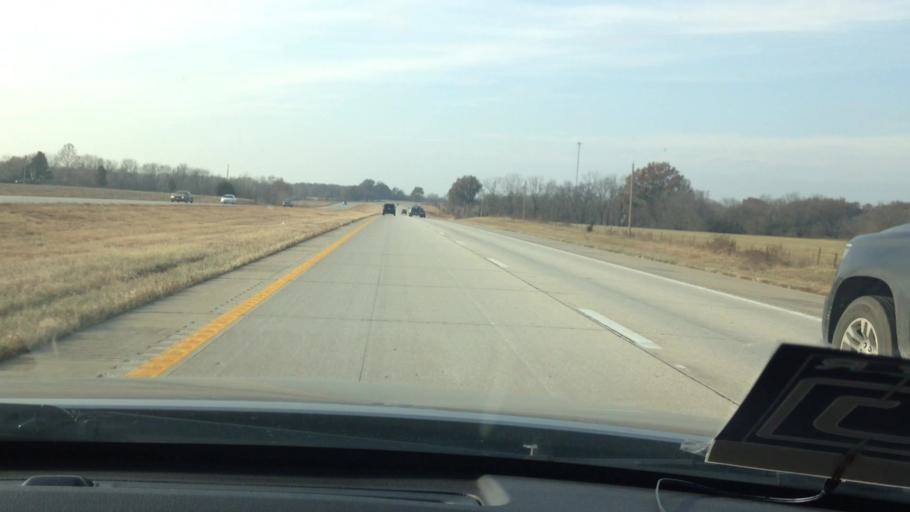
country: US
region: Missouri
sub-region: Henry County
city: Clinton
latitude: 38.4382
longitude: -93.9430
